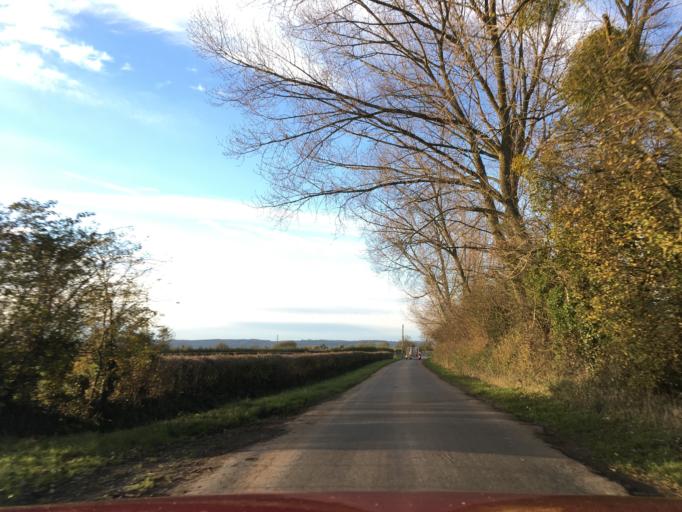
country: GB
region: England
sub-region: South Gloucestershire
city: Hill
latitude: 51.6540
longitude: -2.5243
